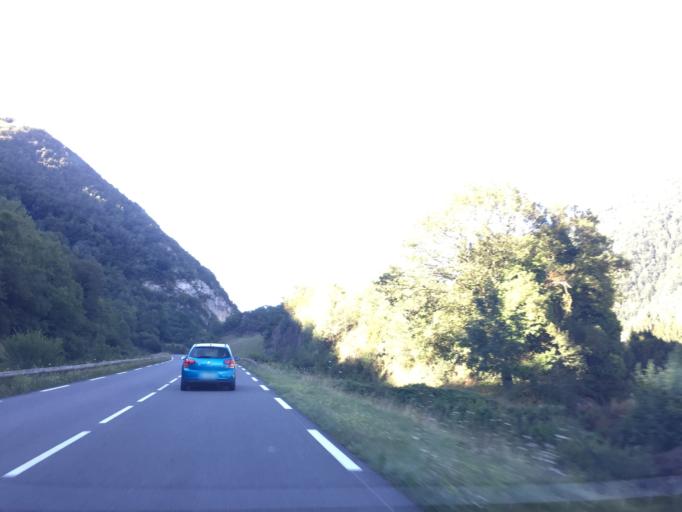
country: FR
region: Midi-Pyrenees
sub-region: Departement des Hautes-Pyrenees
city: Saint-Lary-Soulan
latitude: 42.8892
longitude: 0.3528
